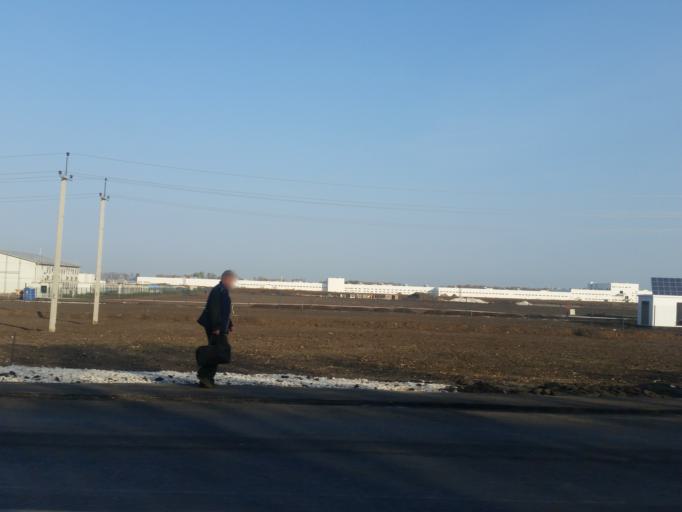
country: RU
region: Ulyanovsk
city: Mirnyy
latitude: 54.3646
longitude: 48.7012
